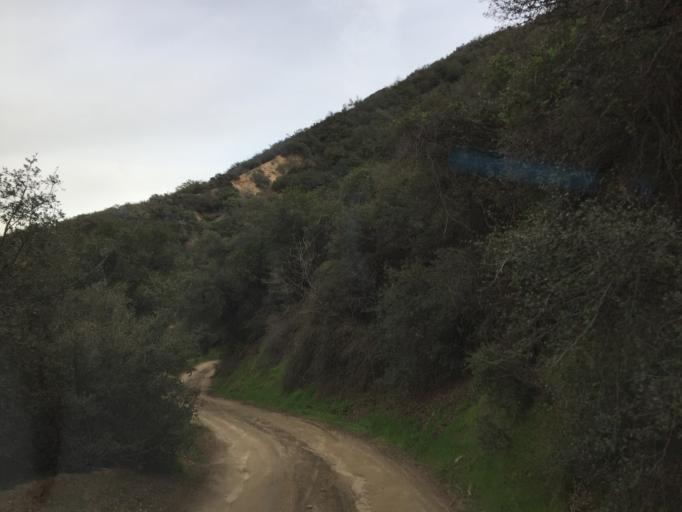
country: US
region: California
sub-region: San Bernardino County
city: Yucaipa
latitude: 34.1160
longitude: -117.0503
